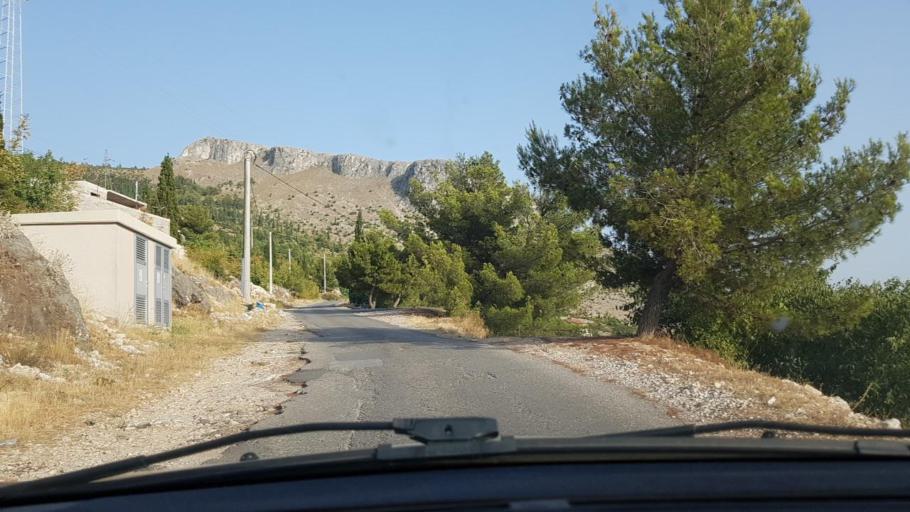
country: BA
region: Federation of Bosnia and Herzegovina
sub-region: Hercegovacko-Bosanski Kanton
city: Mostar
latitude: 43.3494
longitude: 17.8193
